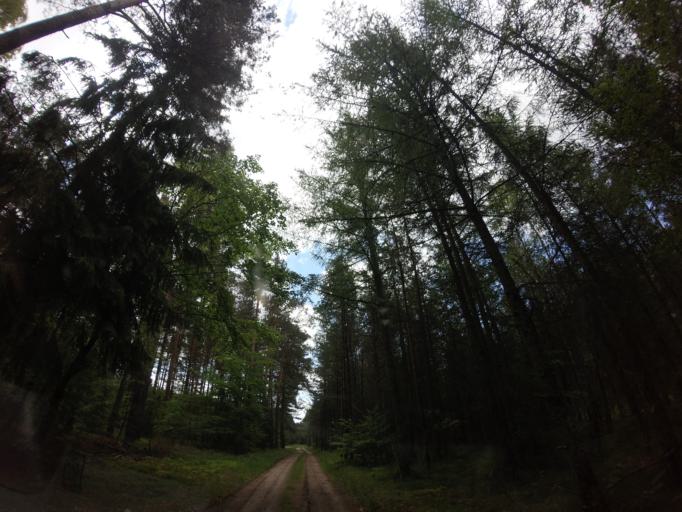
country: PL
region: West Pomeranian Voivodeship
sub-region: Powiat choszczenski
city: Drawno
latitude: 53.2011
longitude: 15.6986
